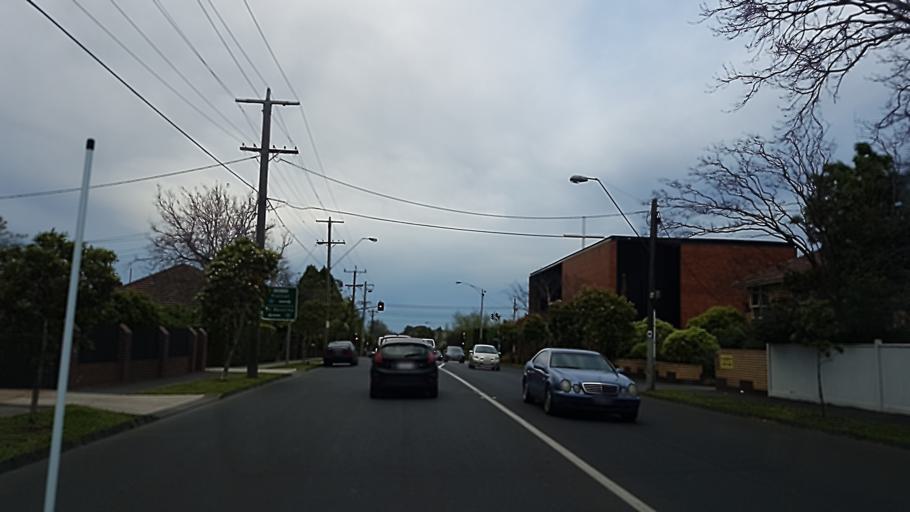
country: AU
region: Victoria
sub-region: Stonnington
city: Glen Iris
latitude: -37.8585
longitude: 145.0515
